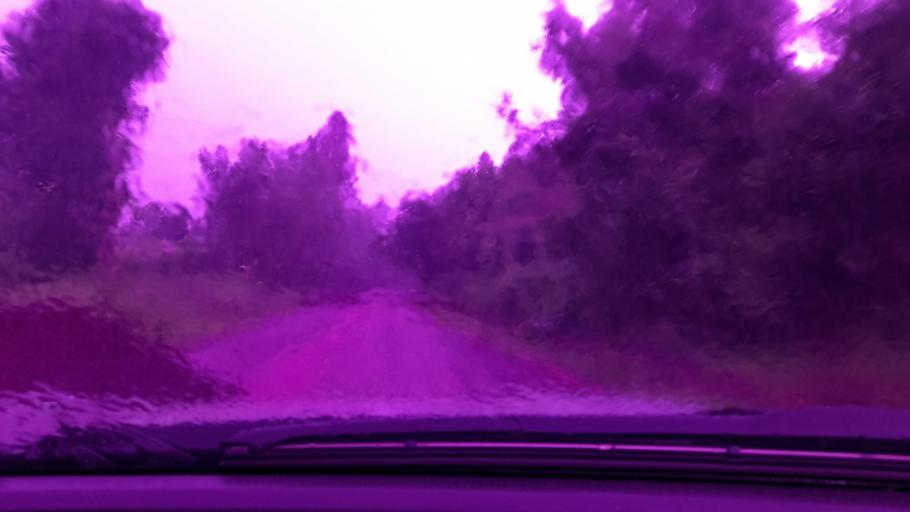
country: ET
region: Oromiya
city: Metu
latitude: 8.3628
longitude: 35.5943
